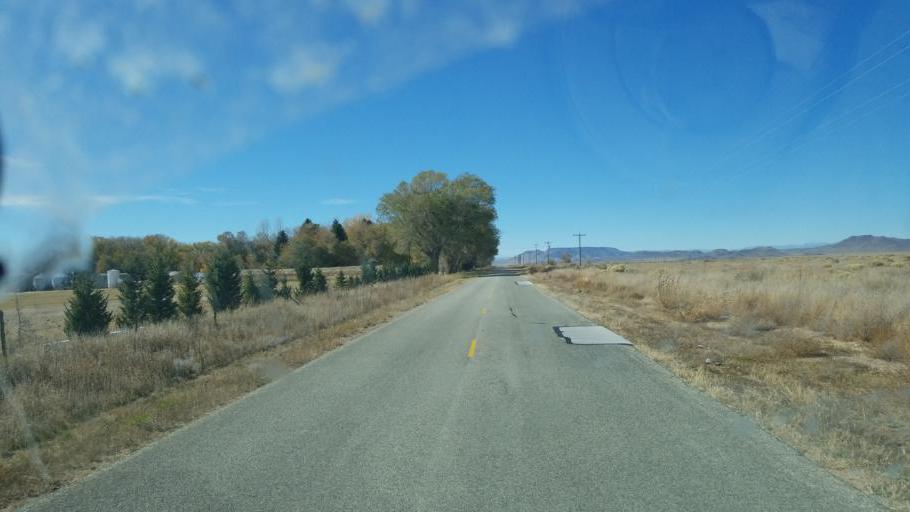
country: US
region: Colorado
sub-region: Costilla County
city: San Luis
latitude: 37.1849
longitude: -105.5511
